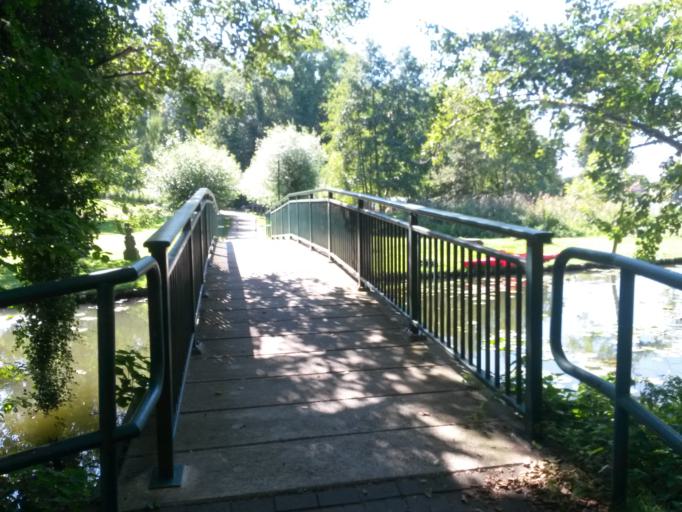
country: DE
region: Brandenburg
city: Lychen
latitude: 53.2120
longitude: 13.3121
